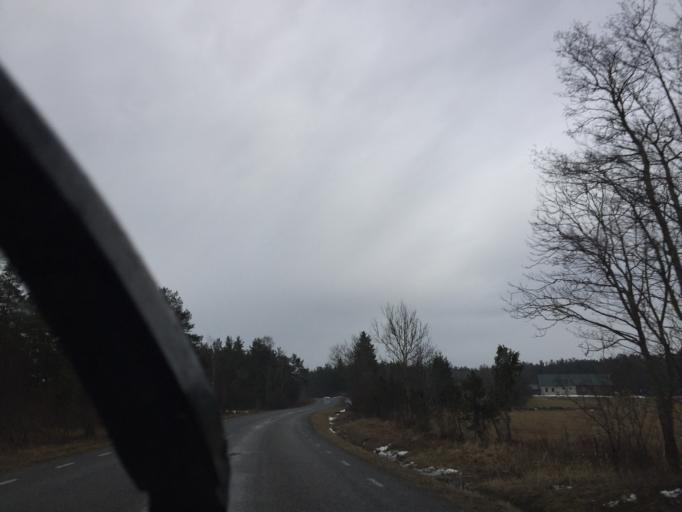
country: EE
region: Saare
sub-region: Orissaare vald
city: Orissaare
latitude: 58.6023
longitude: 22.9750
